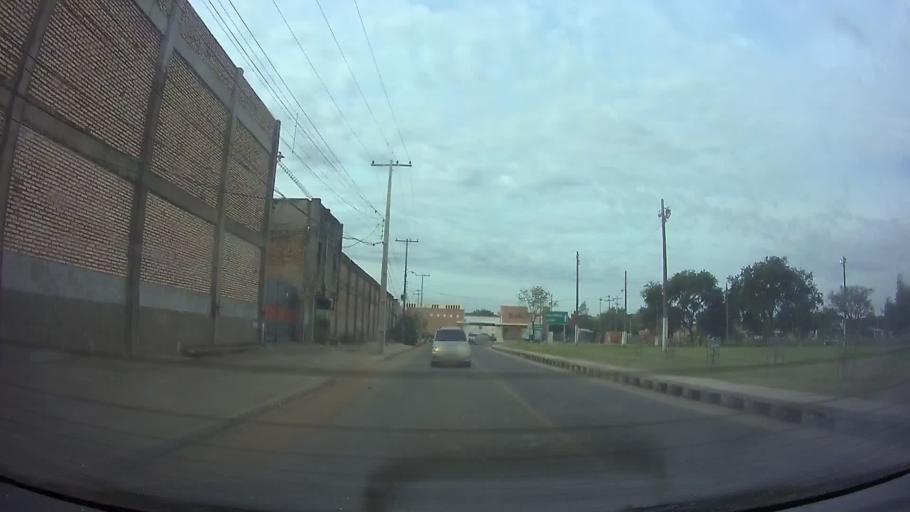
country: PY
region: Central
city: Fernando de la Mora
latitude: -25.2908
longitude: -57.5435
